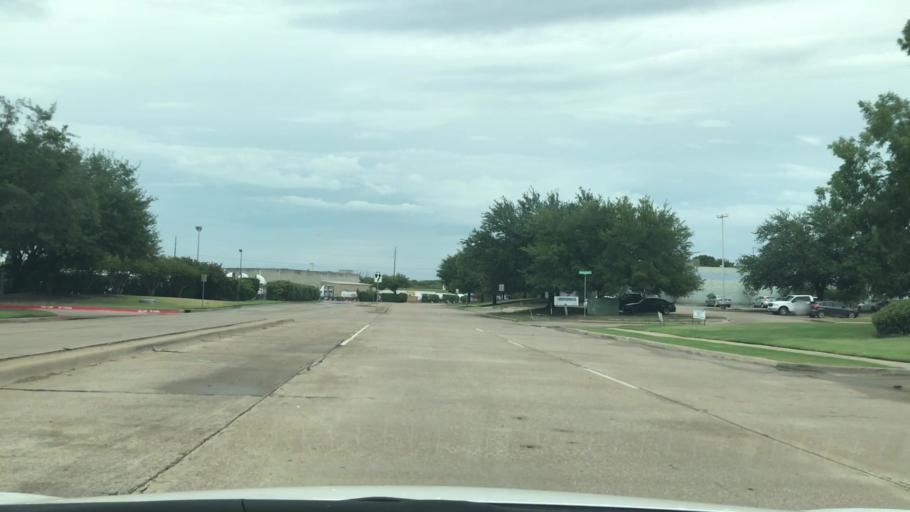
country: US
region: Texas
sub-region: Dallas County
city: Irving
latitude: 32.8423
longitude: -96.8959
